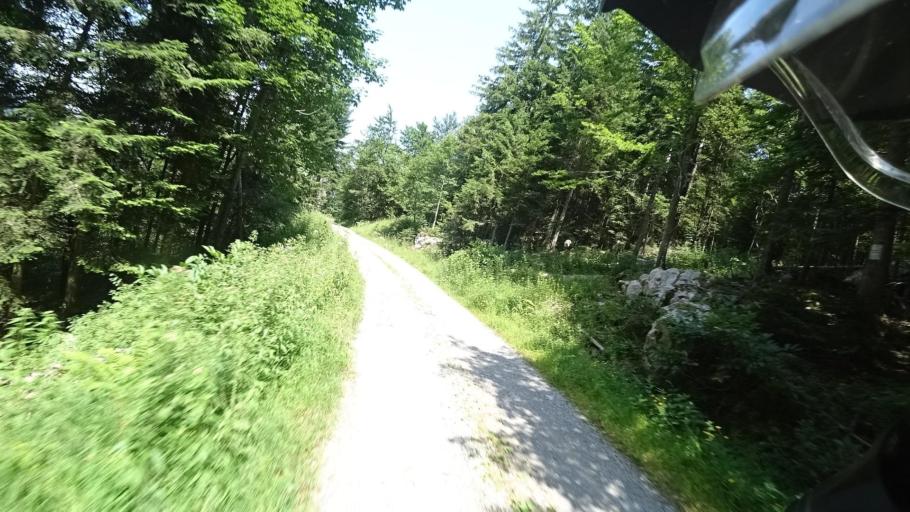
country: HR
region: Primorsko-Goranska
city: Vrbovsko
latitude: 45.3355
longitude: 15.0223
